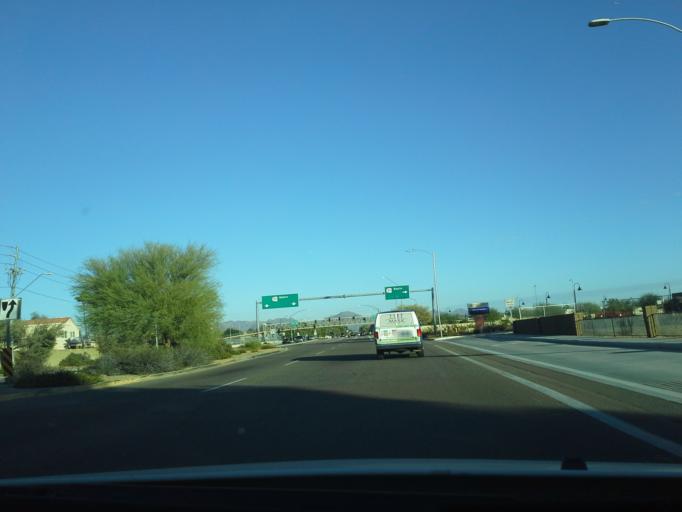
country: US
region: Arizona
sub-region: Maricopa County
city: Paradise Valley
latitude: 33.6550
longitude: -112.0027
